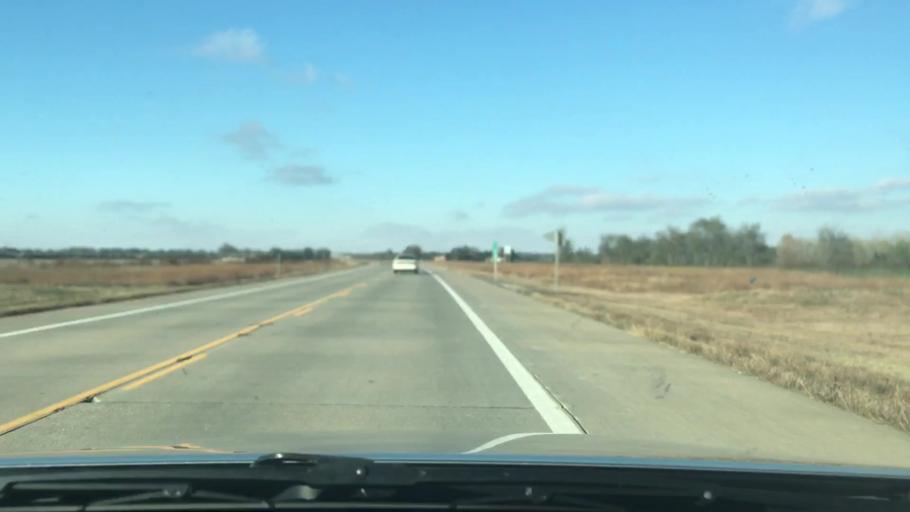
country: US
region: Kansas
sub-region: Reno County
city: Hutchinson
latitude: 38.0640
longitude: -97.9859
